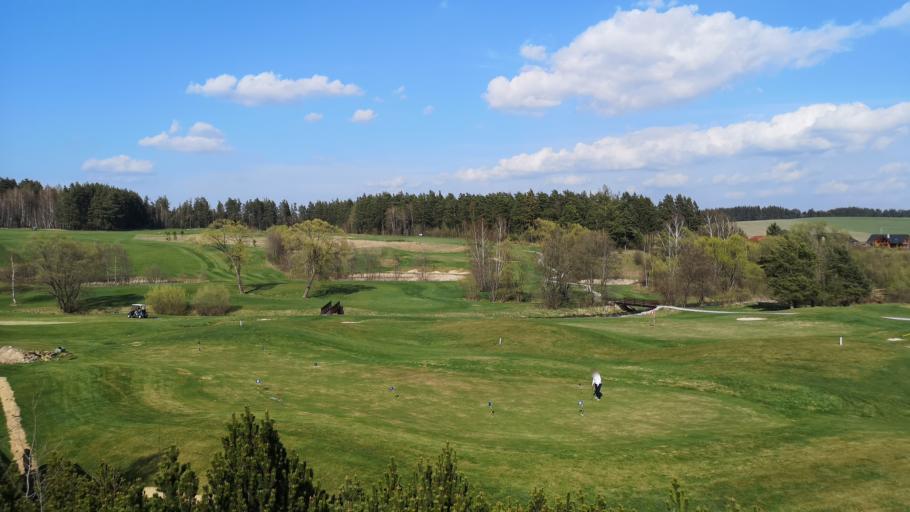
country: SK
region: Presovsky
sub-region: Okres Poprad
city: Nova Lesna
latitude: 49.1369
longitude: 20.3405
